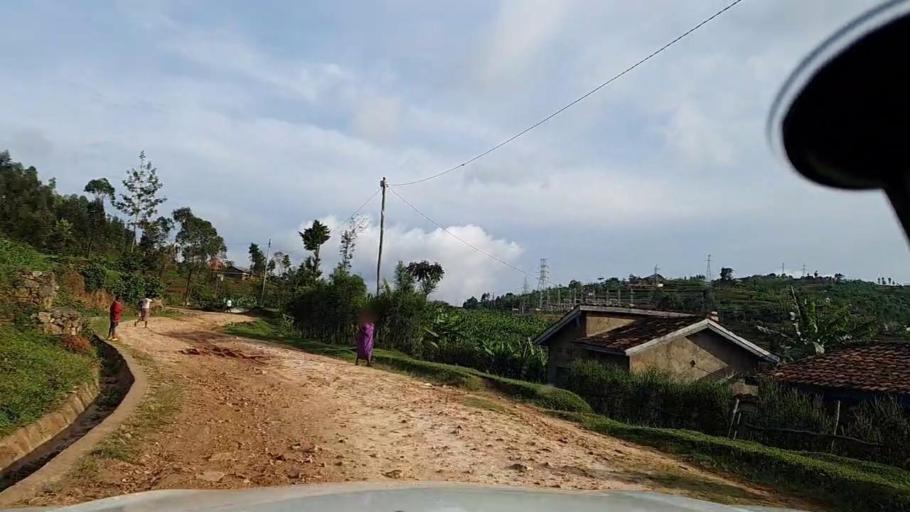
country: RW
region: Southern Province
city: Gitarama
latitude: -2.1832
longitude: 29.5631
